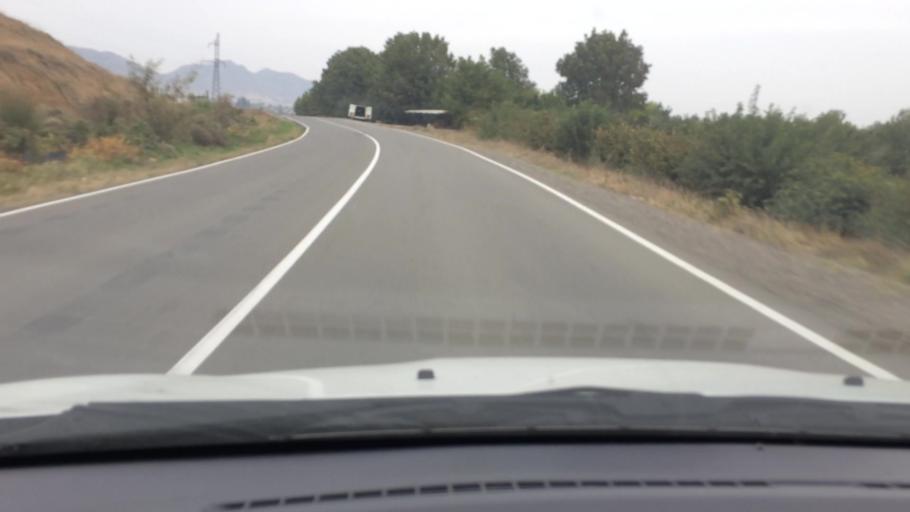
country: AM
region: Tavush
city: Bagratashen
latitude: 41.2846
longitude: 44.7905
